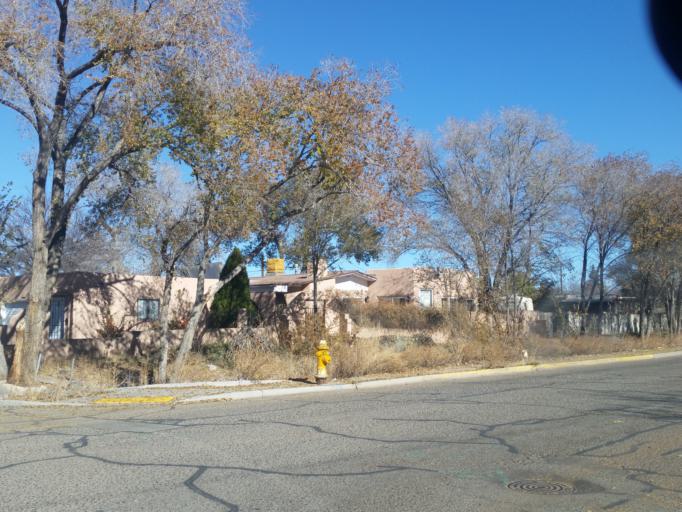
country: US
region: New Mexico
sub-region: Santa Fe County
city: Santa Fe
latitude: 35.6625
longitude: -105.9675
